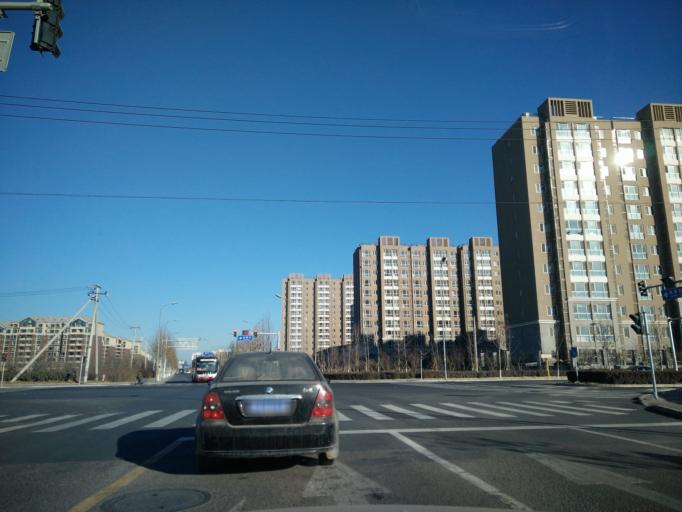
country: CN
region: Beijing
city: Yinghai
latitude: 39.7081
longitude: 116.3981
